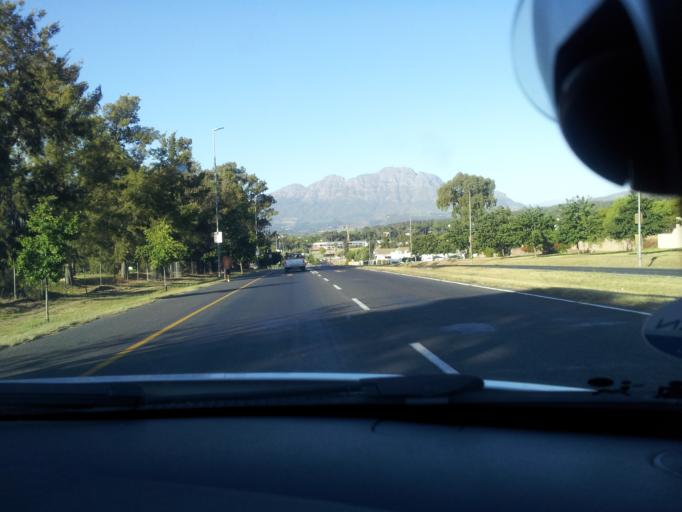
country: ZA
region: Western Cape
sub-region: Cape Winelands District Municipality
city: Stellenbosch
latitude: -33.9610
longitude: 18.8519
